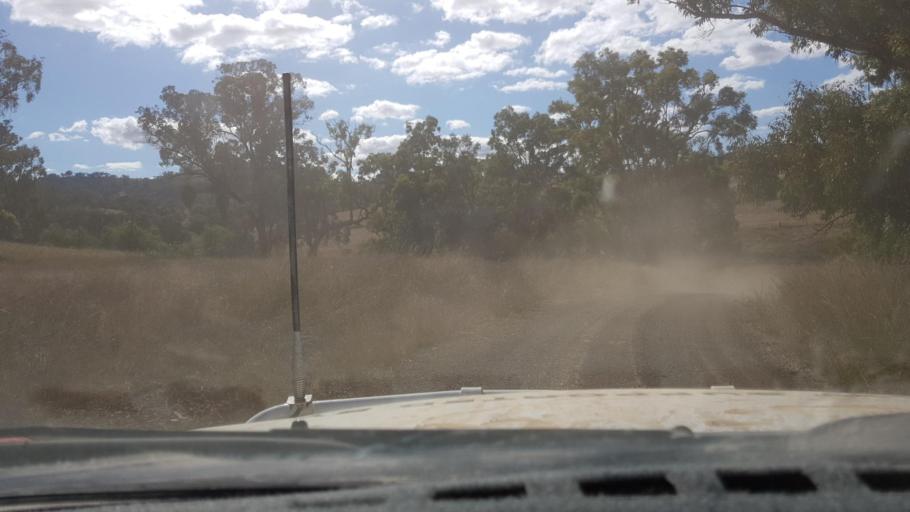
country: AU
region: New South Wales
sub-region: Tamworth Municipality
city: Manilla
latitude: -30.4492
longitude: 150.7798
